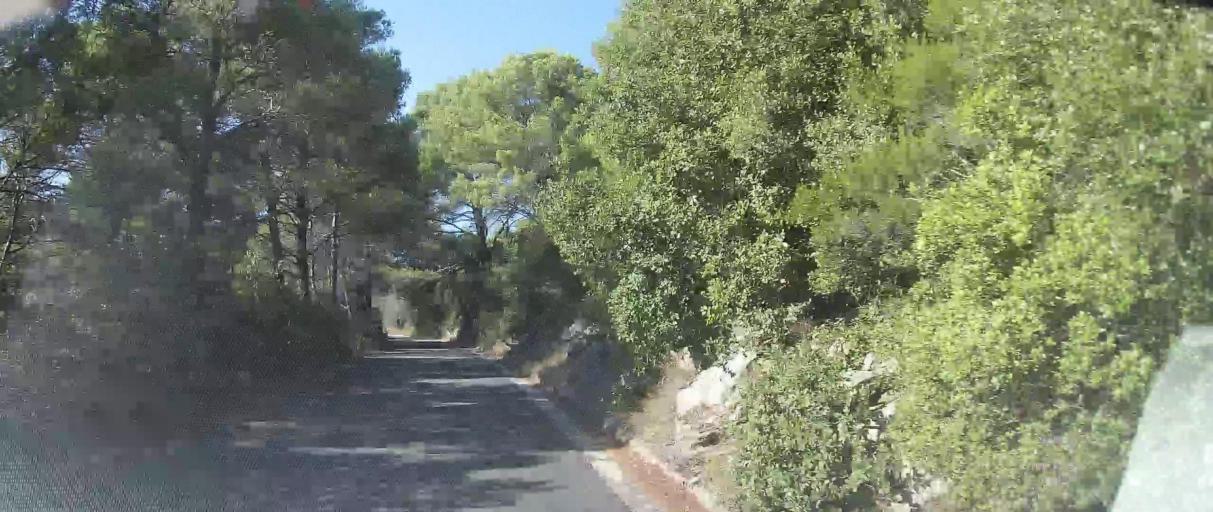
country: HR
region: Dubrovacko-Neretvanska
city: Blato
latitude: 42.7853
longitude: 17.3684
